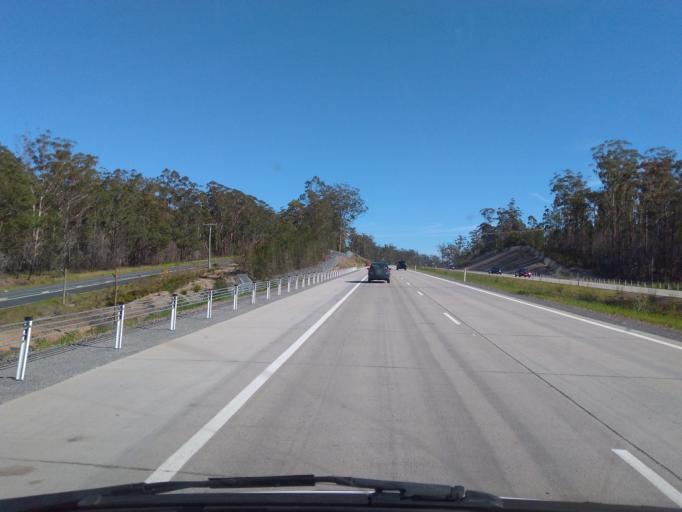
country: AU
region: New South Wales
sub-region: Kempsey
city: Kempsey
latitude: -31.1724
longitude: 152.8228
